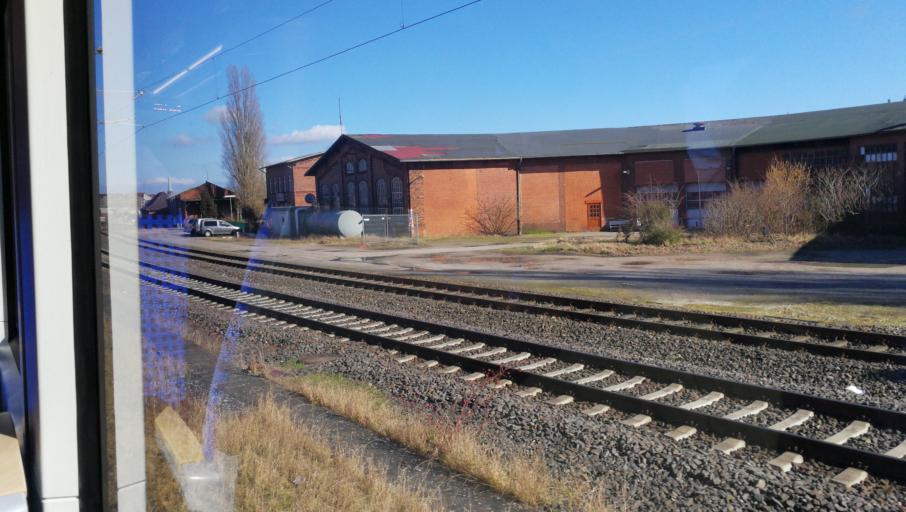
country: DE
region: Schleswig-Holstein
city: Luebeck
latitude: 53.8627
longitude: 10.6578
